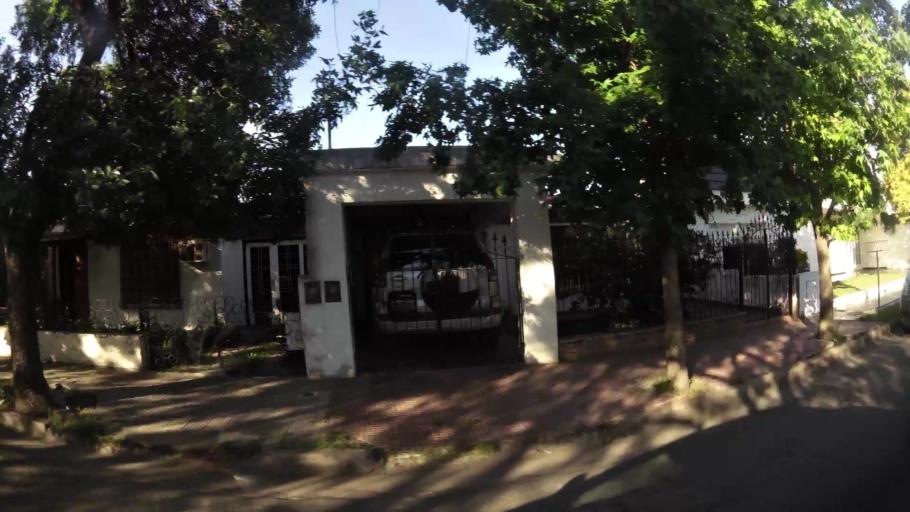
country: AR
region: Cordoba
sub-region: Departamento de Capital
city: Cordoba
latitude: -31.3812
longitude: -64.2343
